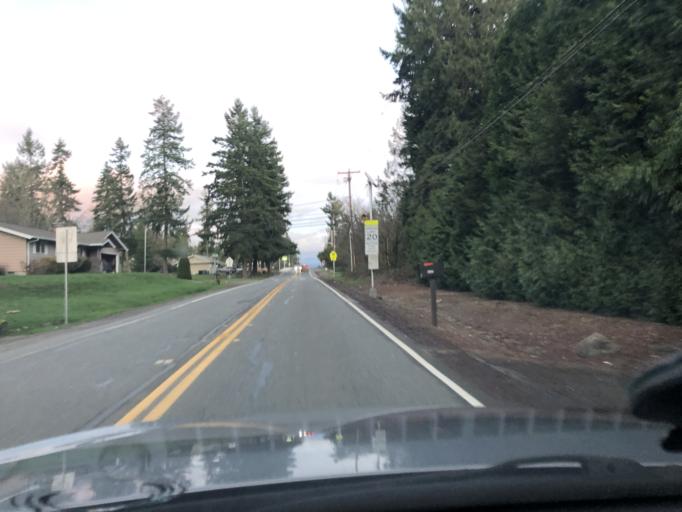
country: US
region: Washington
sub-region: King County
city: Lakeland North
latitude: 47.3187
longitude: -122.2678
